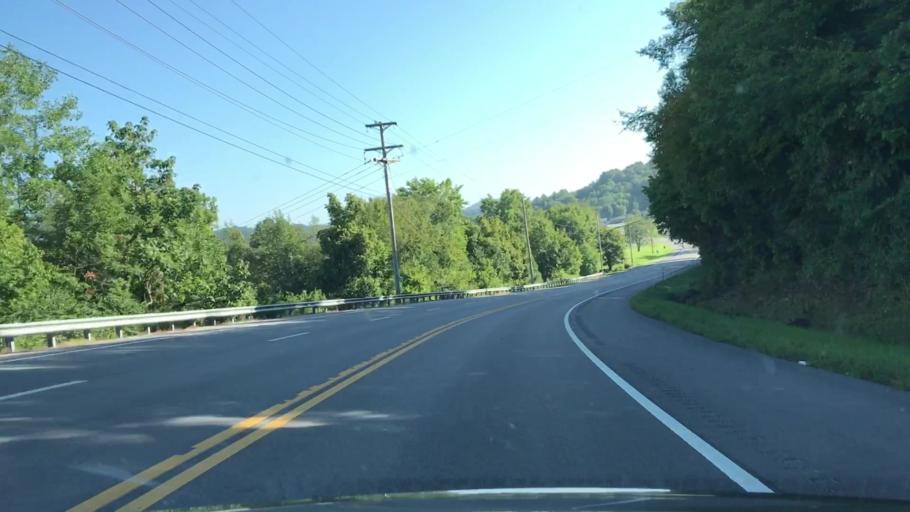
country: US
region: Tennessee
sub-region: Clay County
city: Celina
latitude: 36.5382
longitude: -85.5070
